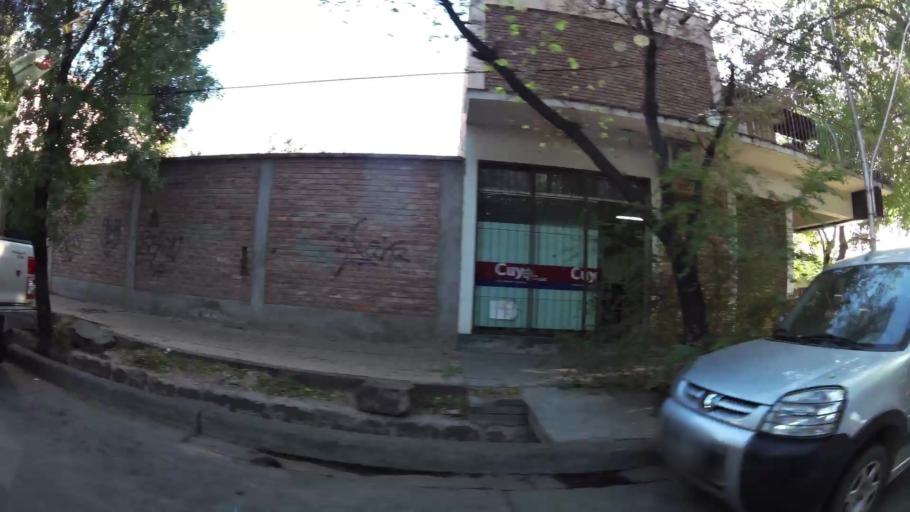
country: AR
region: Mendoza
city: Mendoza
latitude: -32.8721
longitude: -68.8262
